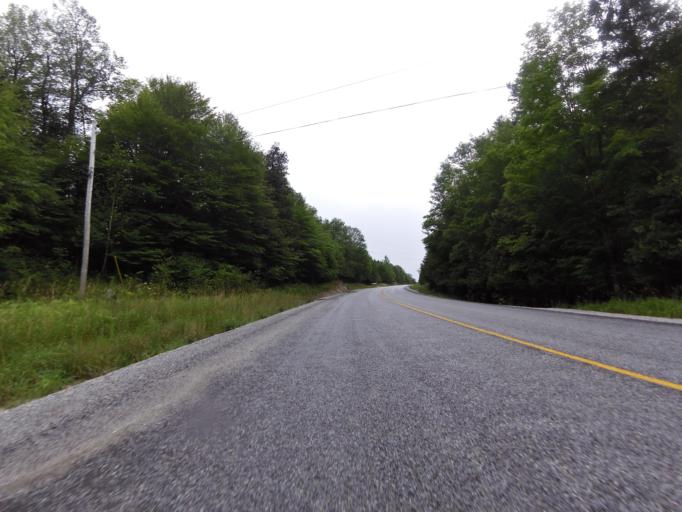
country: CA
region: Ontario
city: Perth
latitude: 44.9118
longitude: -76.4867
